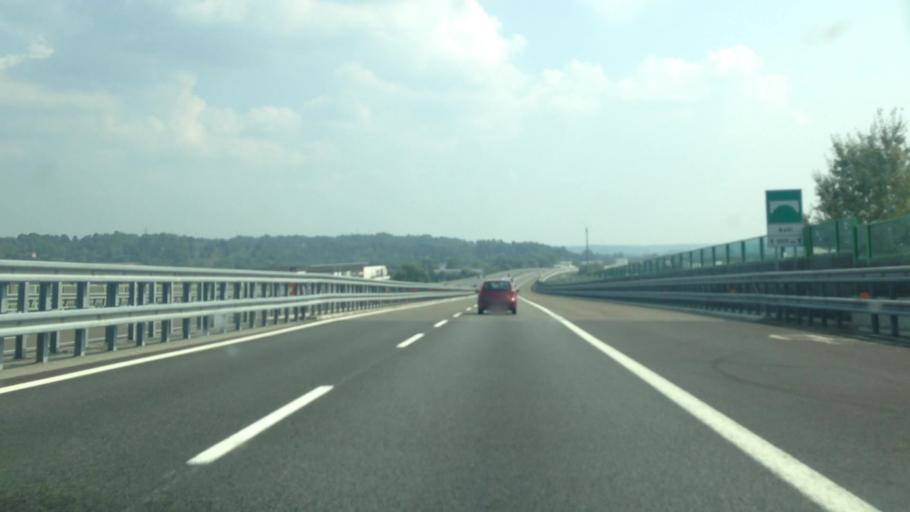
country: IT
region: Piedmont
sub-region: Provincia di Asti
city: Asti
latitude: 44.9155
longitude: 8.2180
